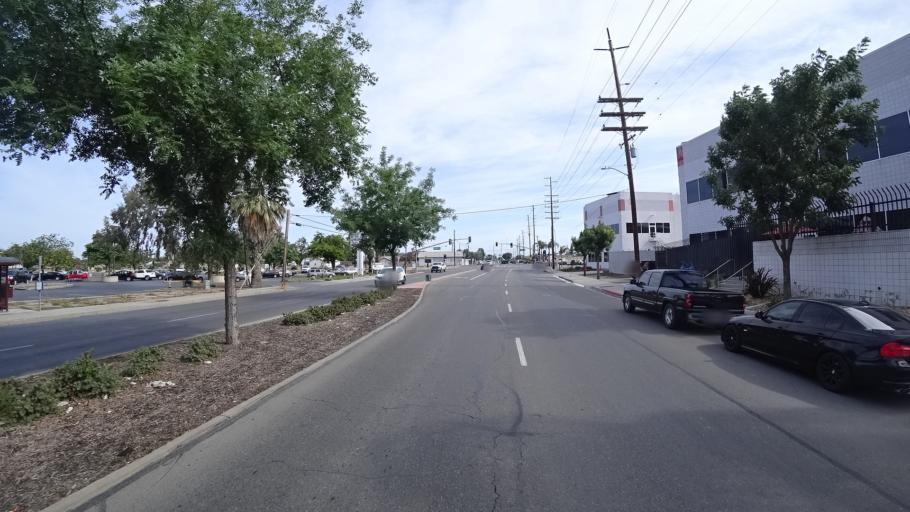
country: US
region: California
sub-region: Kings County
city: Hanford
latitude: 36.3223
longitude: -119.6550
